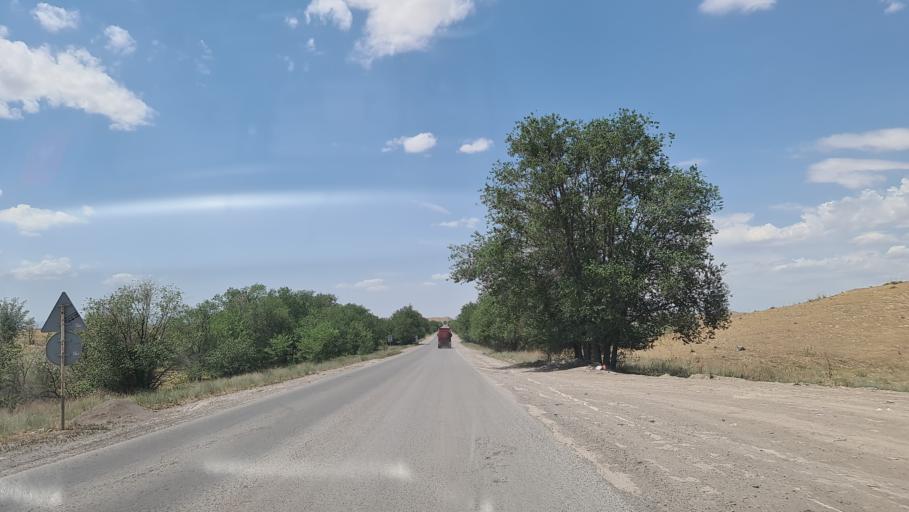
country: KG
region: Chuy
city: Bystrovka
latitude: 43.3228
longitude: 75.9241
